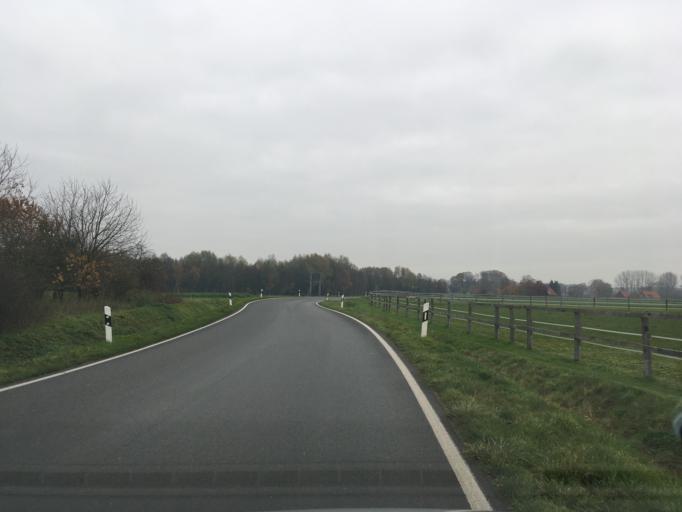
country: DE
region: North Rhine-Westphalia
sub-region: Regierungsbezirk Munster
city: Legden
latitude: 52.0318
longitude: 7.1177
